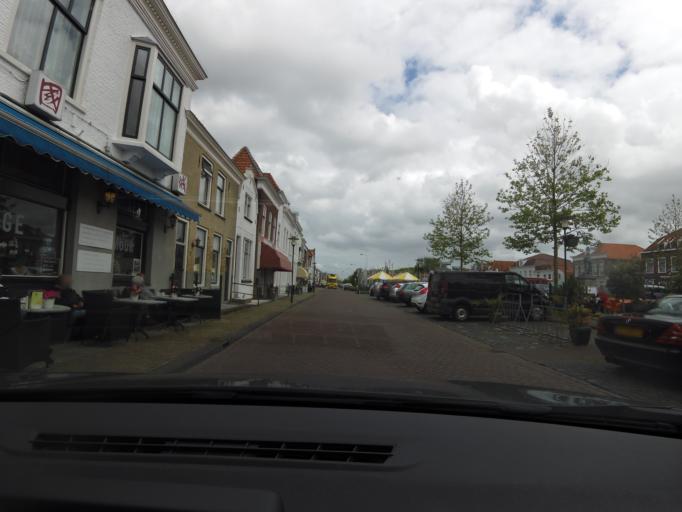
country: NL
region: Zeeland
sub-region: Schouwen-Duiveland
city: Scharendijke
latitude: 51.7257
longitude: 3.9121
